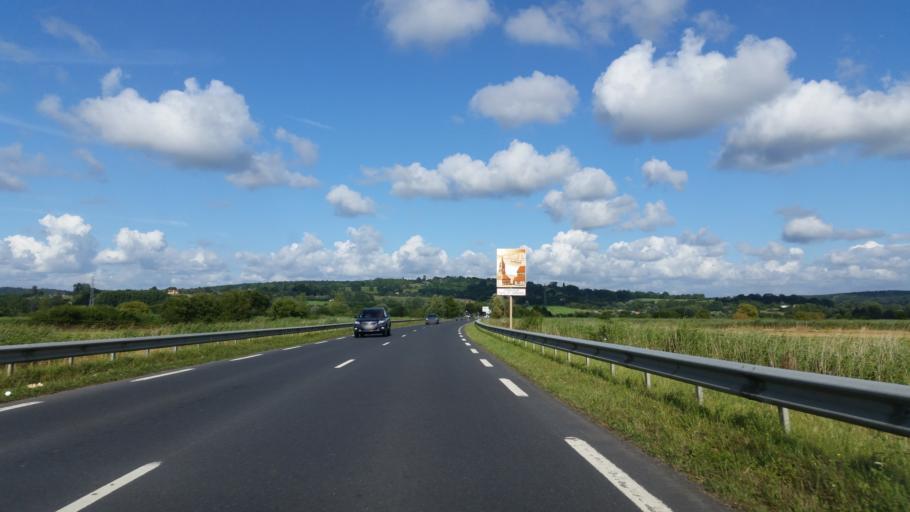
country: FR
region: Lower Normandy
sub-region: Departement du Calvados
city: Touques
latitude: 49.3301
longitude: 0.0996
